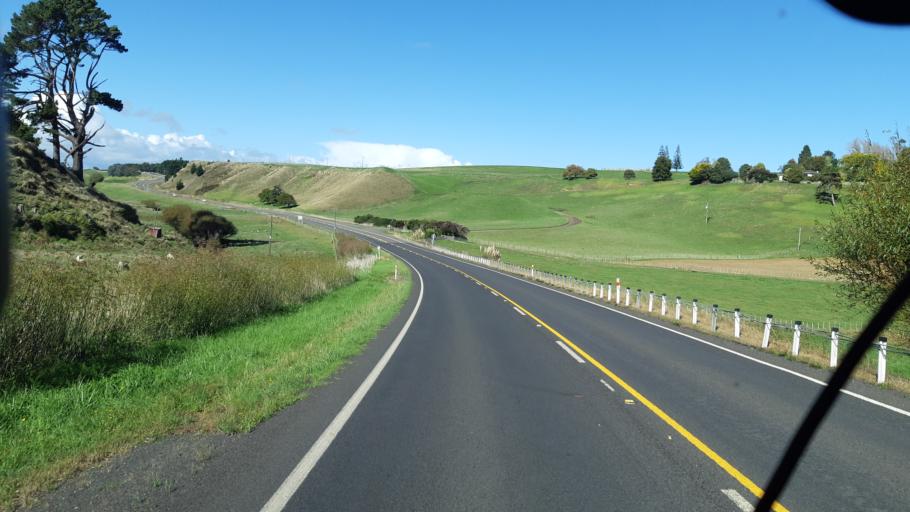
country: NZ
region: Manawatu-Wanganui
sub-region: Wanganui District
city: Wanganui
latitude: -39.9658
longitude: 175.1011
